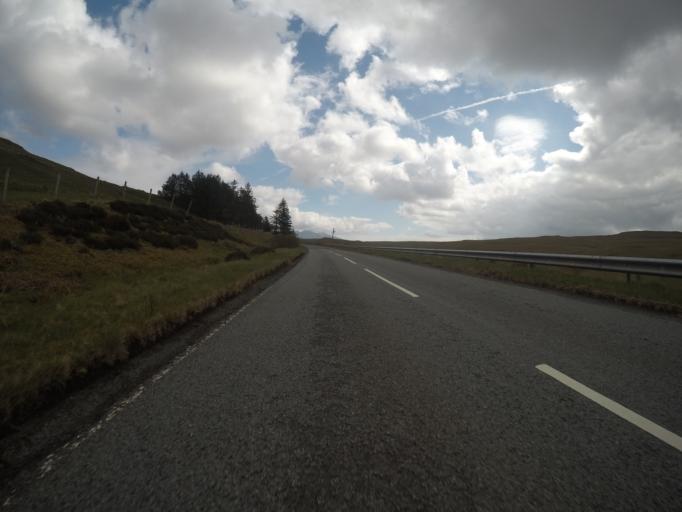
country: GB
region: Scotland
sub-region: Highland
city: Isle of Skye
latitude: 57.3252
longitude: -6.3324
